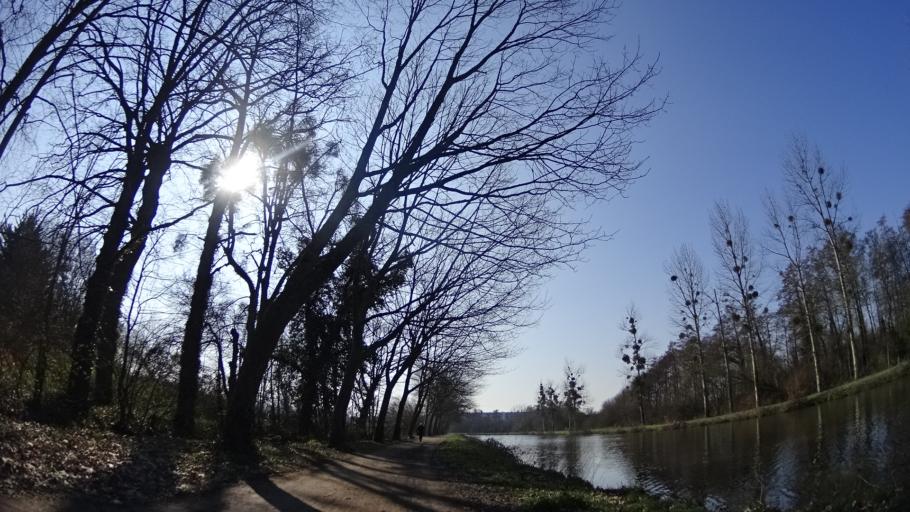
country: FR
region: Brittany
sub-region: Departement d'Ille-et-Vilaine
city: Saint-Gregoire
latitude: 48.1358
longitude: -1.6768
